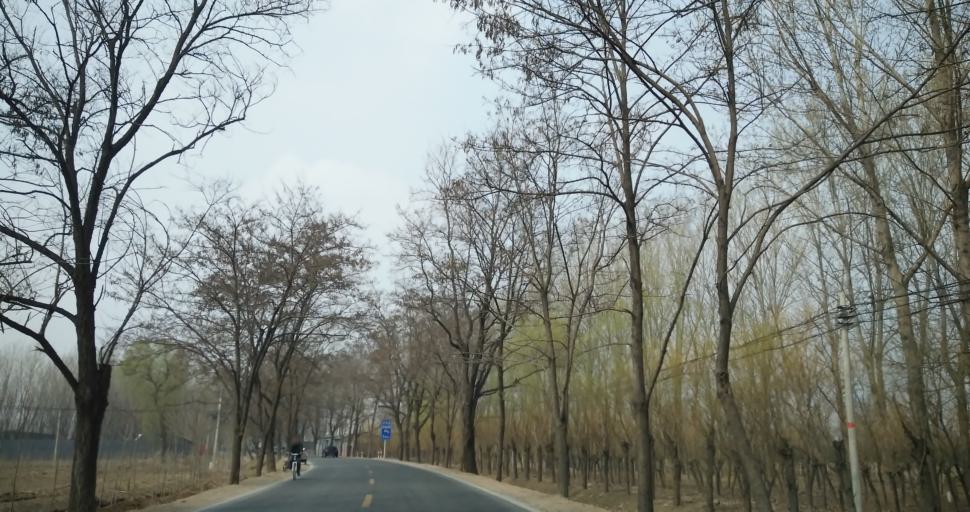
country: CN
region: Beijing
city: Qingyundian
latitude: 39.6879
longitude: 116.5048
